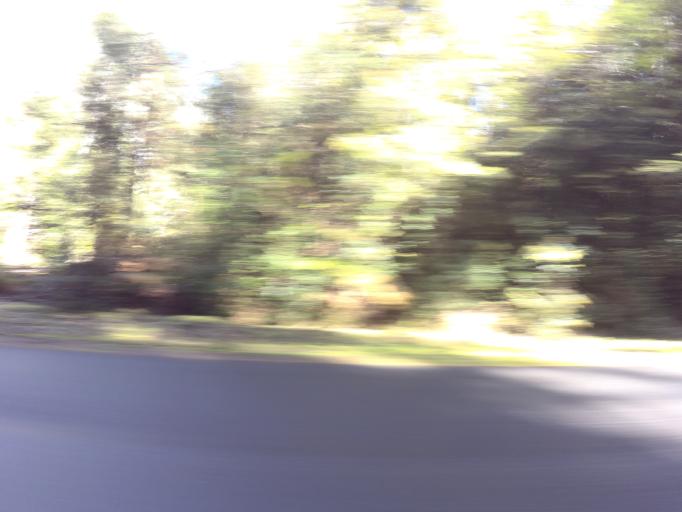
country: AU
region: Tasmania
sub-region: Derwent Valley
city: New Norfolk
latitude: -42.7267
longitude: 146.4324
